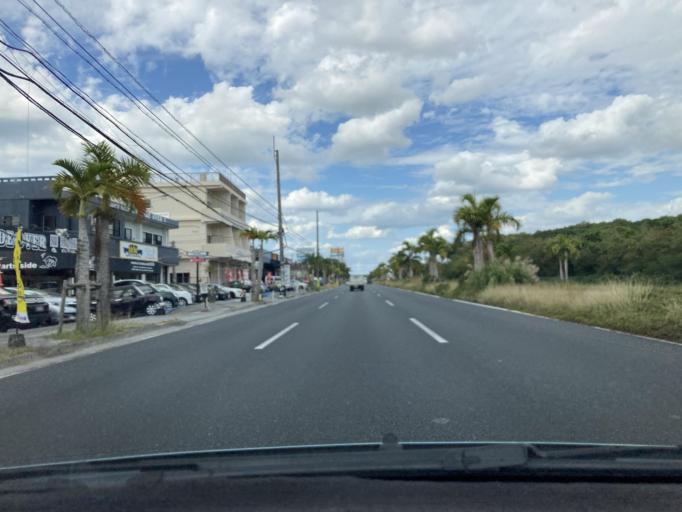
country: JP
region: Okinawa
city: Chatan
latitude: 26.3326
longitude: 127.7515
